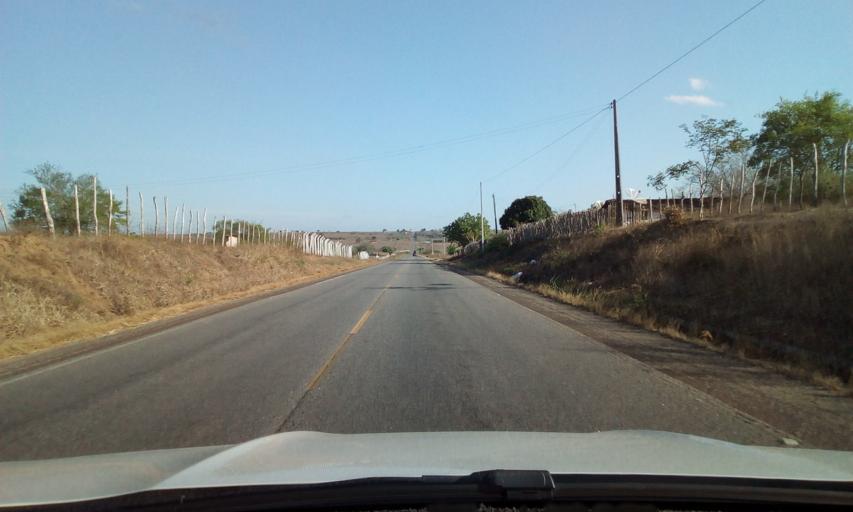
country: BR
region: Paraiba
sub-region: Mulungu
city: Mulungu
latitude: -6.9650
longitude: -35.4081
